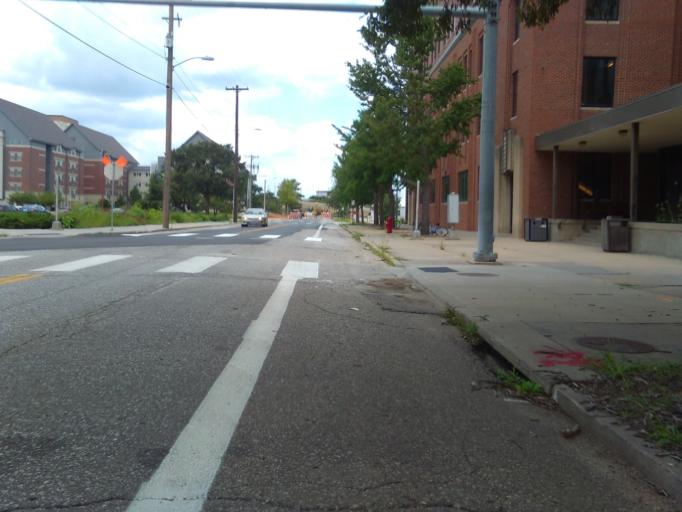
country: US
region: Nebraska
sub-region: Lancaster County
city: Lincoln
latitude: 40.8226
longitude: -96.6981
